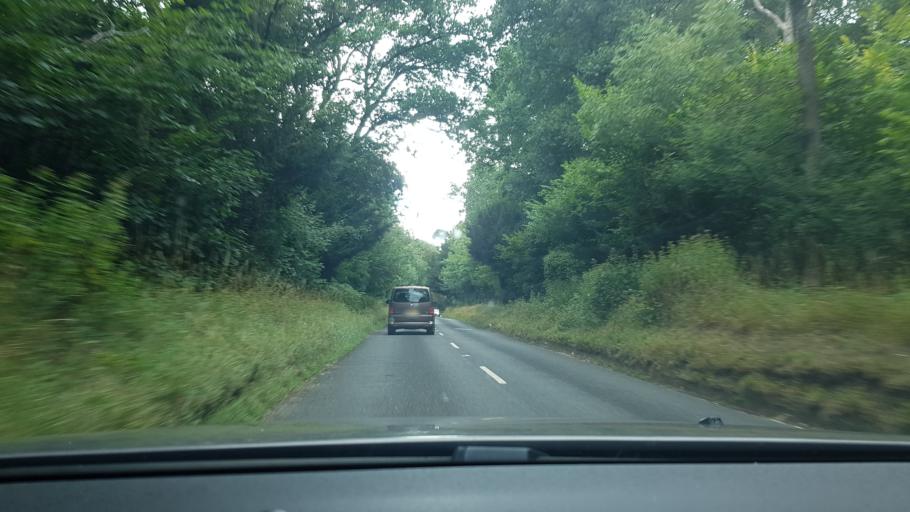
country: GB
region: England
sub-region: West Berkshire
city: Basildon
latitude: 51.4730
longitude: -1.1616
